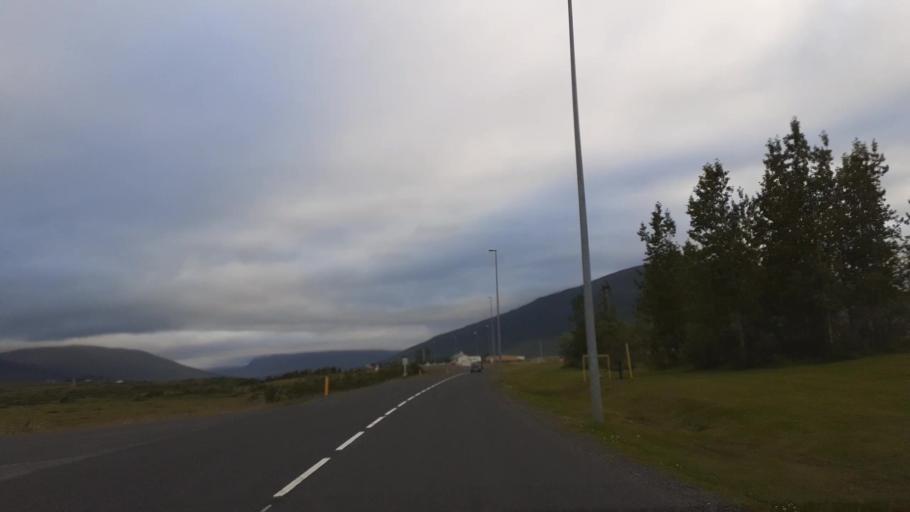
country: IS
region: Northeast
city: Dalvik
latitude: 65.9672
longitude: -18.5300
